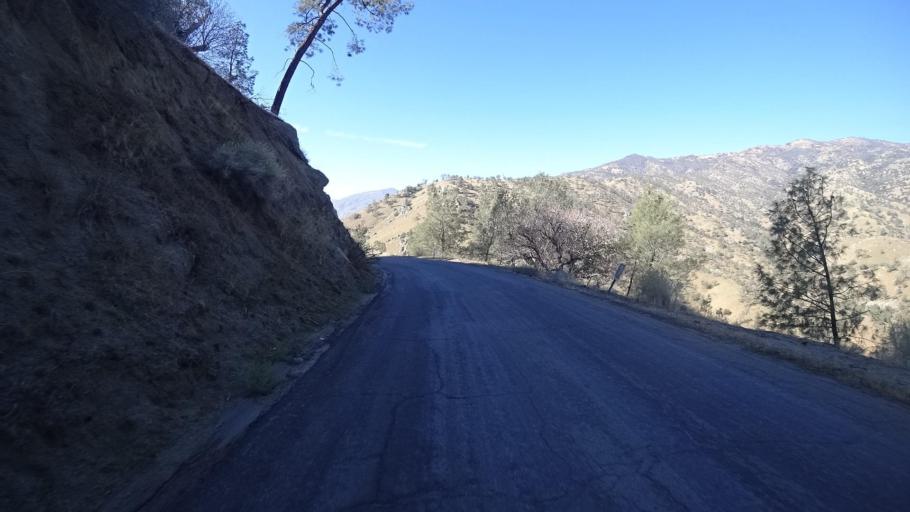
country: US
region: California
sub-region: Kern County
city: Bodfish
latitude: 35.5465
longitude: -118.6139
